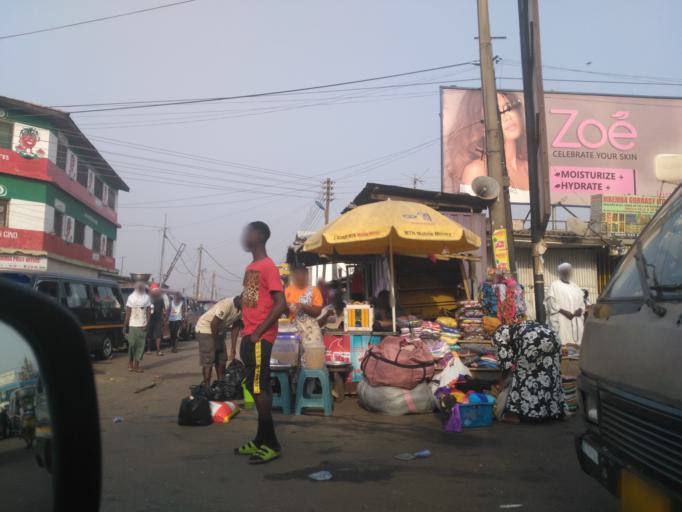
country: GH
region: Greater Accra
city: Accra
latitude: 5.5815
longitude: -0.1988
